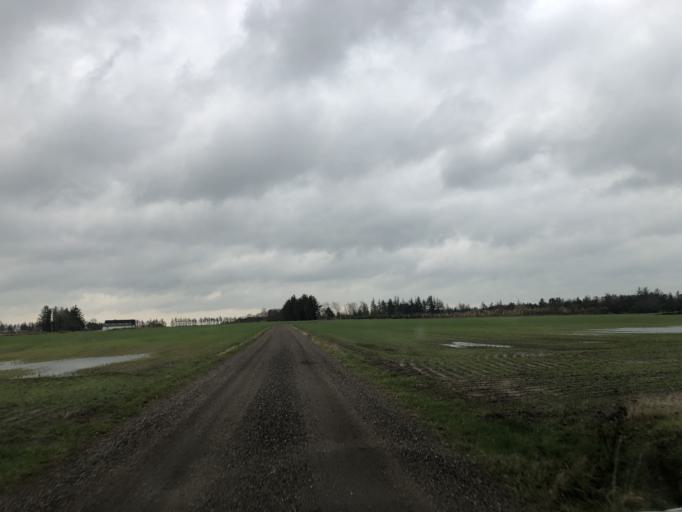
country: DK
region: Central Jutland
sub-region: Holstebro Kommune
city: Ulfborg
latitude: 56.3085
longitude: 8.2020
